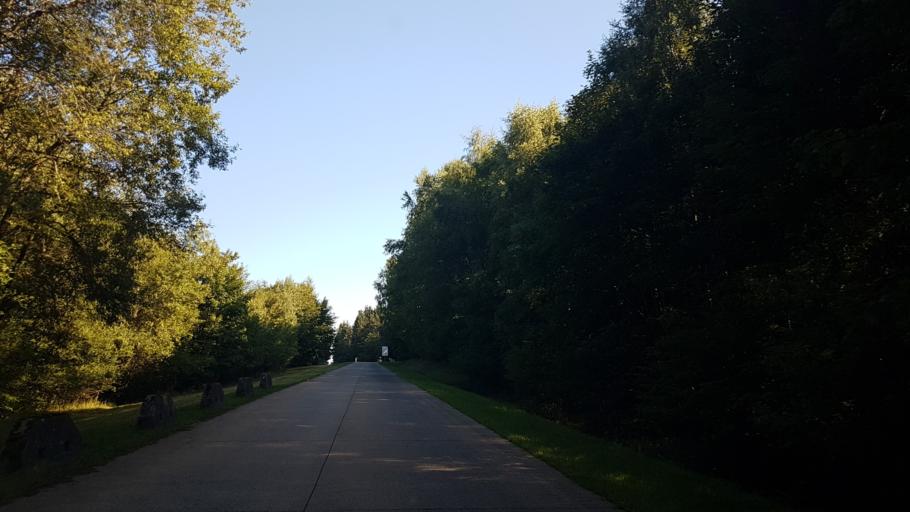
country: DE
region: Rheinland-Pfalz
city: Reichenbach
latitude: 49.6369
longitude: 7.3090
